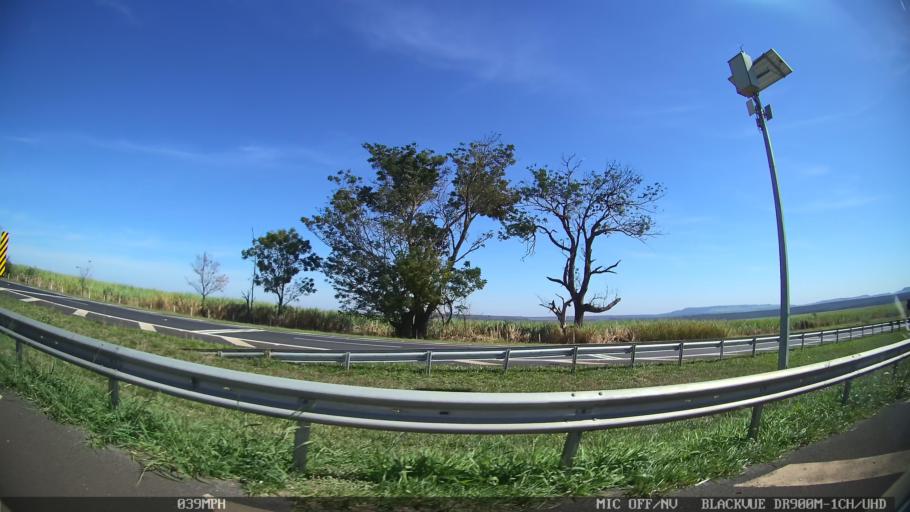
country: BR
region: Sao Paulo
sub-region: Santa Rita Do Passa Quatro
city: Santa Rita do Passa Quatro
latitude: -21.6558
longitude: -47.6095
